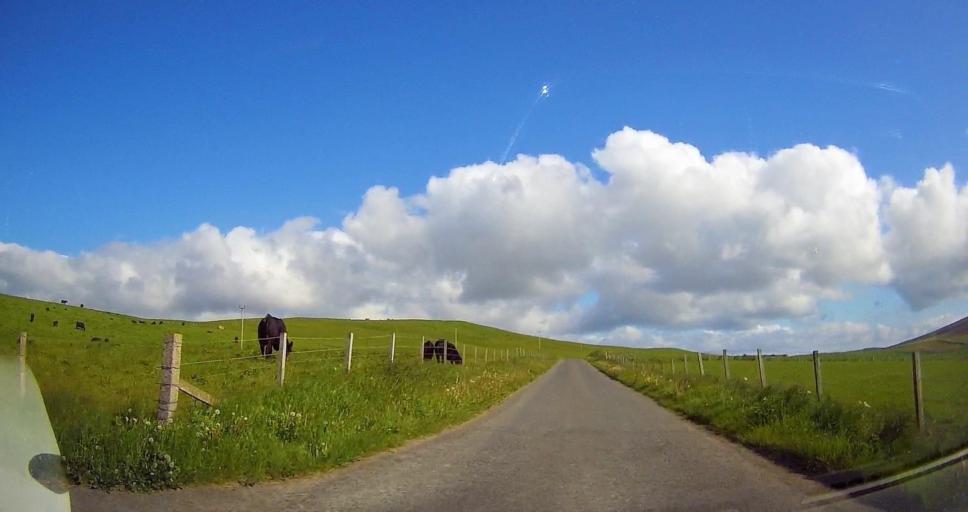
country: GB
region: Scotland
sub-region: Orkney Islands
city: Stromness
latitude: 58.9816
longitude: -3.1389
